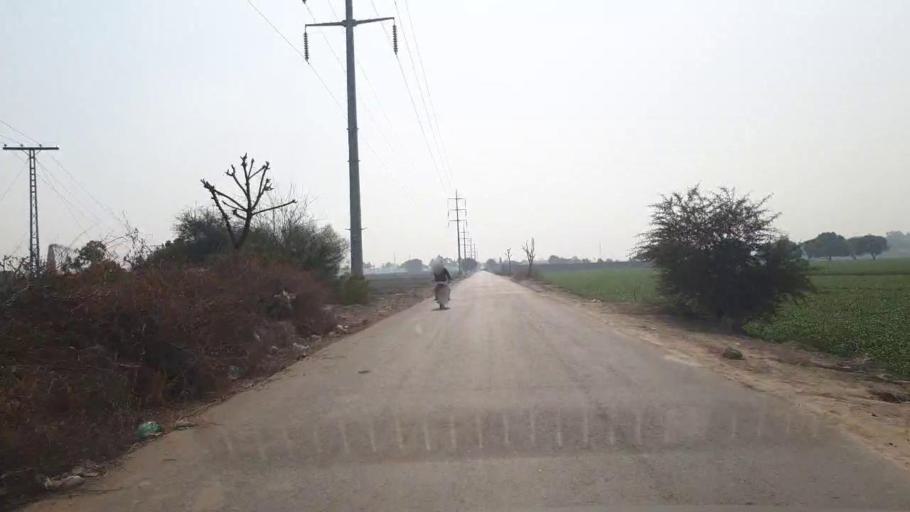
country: PK
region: Sindh
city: Hala
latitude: 25.8317
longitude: 68.4200
